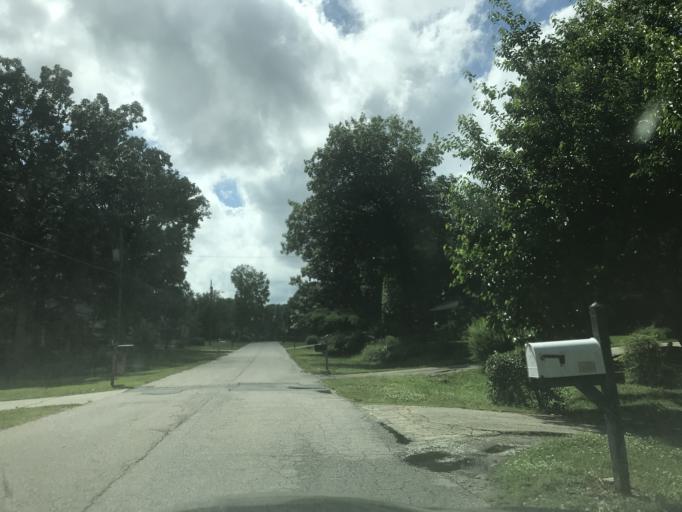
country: US
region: North Carolina
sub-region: Wake County
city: Raleigh
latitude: 35.8061
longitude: -78.5668
